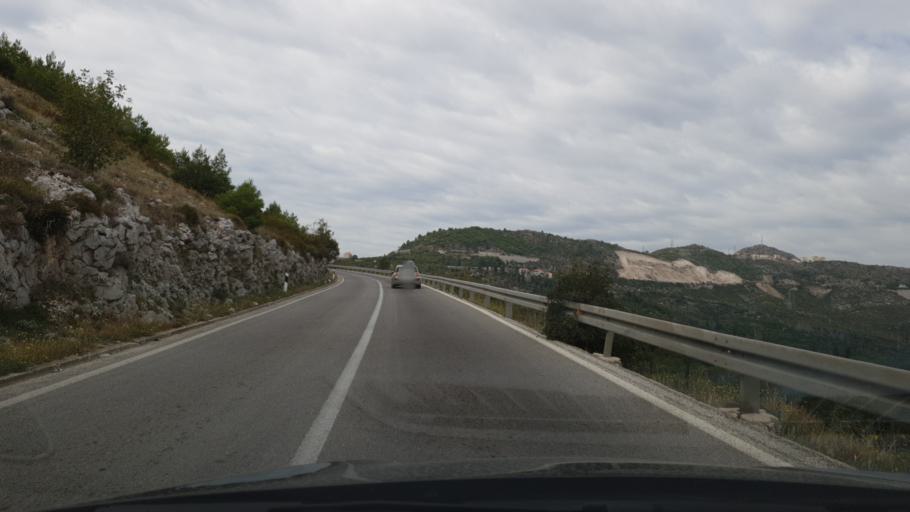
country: HR
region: Dubrovacko-Neretvanska
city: Cibaca
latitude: 42.6410
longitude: 18.1675
